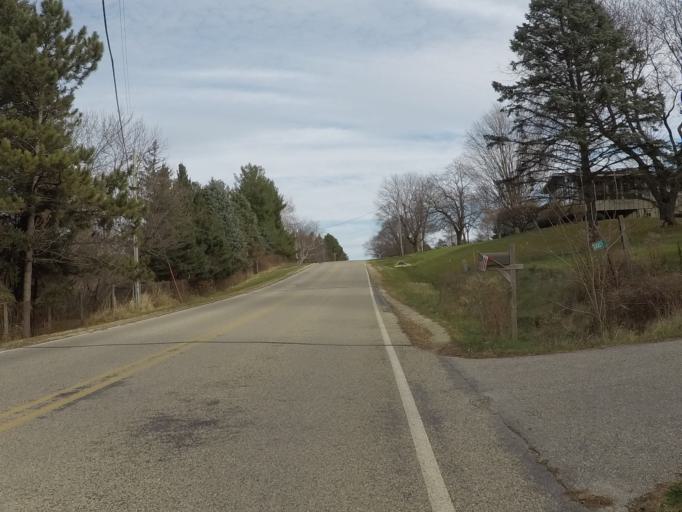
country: US
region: Wisconsin
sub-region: Dane County
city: Middleton
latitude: 43.0820
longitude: -89.5642
